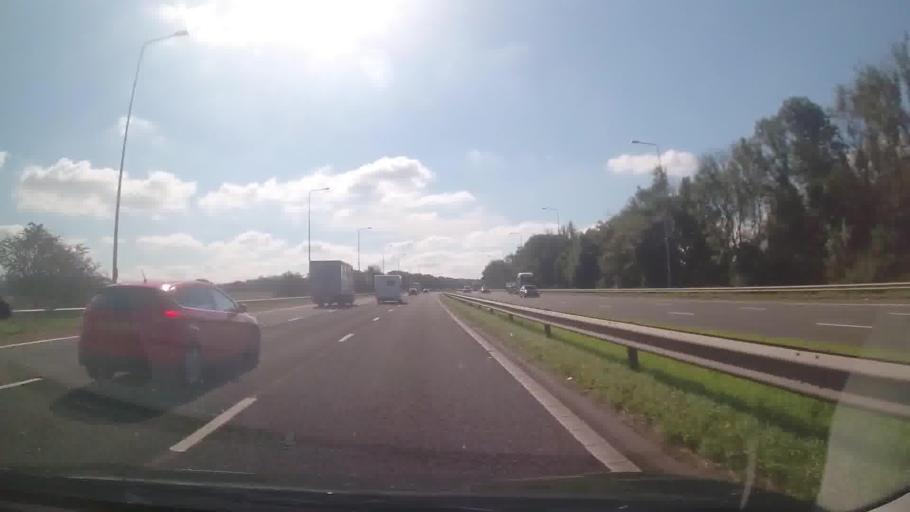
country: GB
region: England
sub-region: Lancashire
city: Coppull
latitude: 53.6158
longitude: -2.6857
